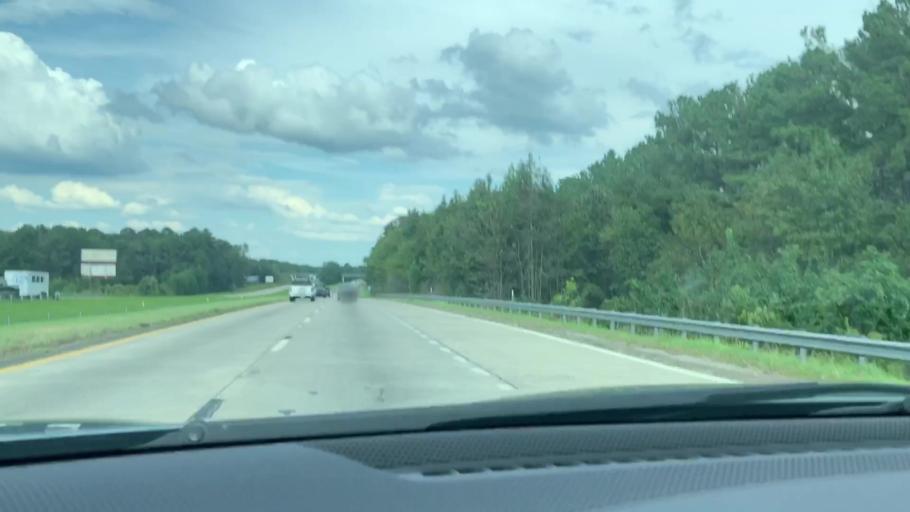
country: US
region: South Carolina
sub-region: Hampton County
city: Yemassee
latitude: 32.7052
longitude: -80.8700
